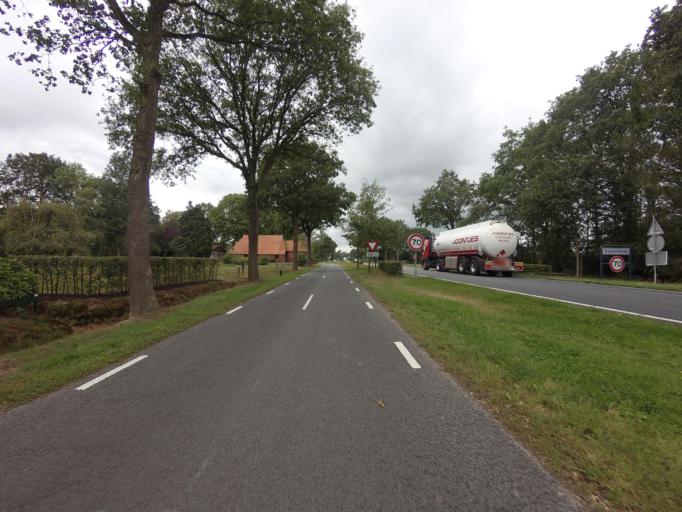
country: NL
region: Friesland
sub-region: Gemeente Heerenveen
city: Jubbega
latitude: 52.9594
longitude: 6.1920
